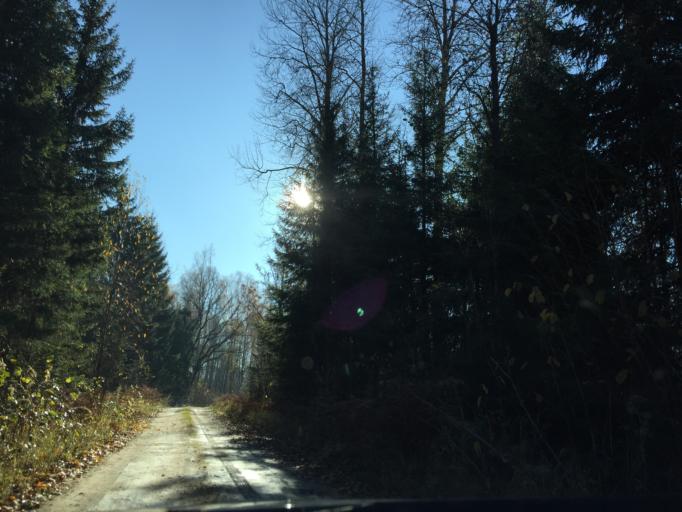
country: LV
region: Aizkraukles Rajons
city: Aizkraukle
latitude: 56.7131
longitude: 25.2999
